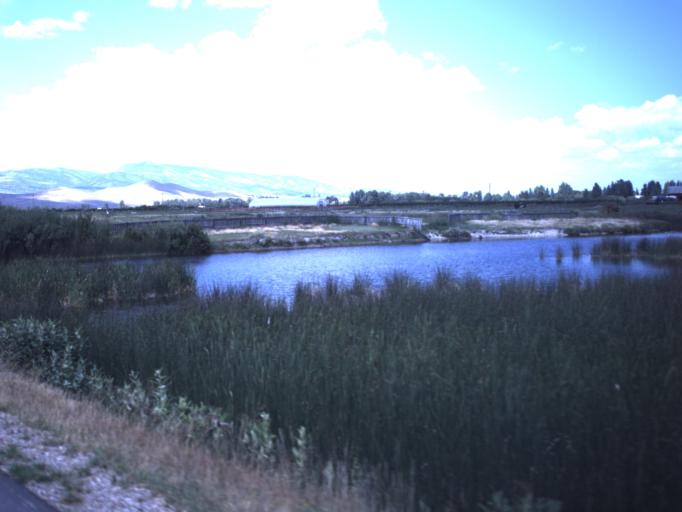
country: US
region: Utah
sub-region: Rich County
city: Randolph
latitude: 41.8356
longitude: -111.3321
